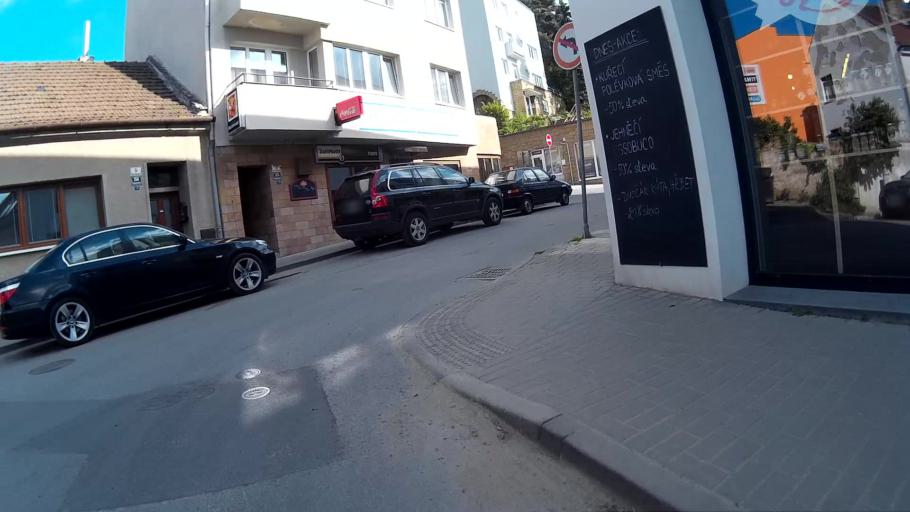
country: CZ
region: South Moravian
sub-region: Mesto Brno
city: Brno
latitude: 49.2119
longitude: 16.5788
